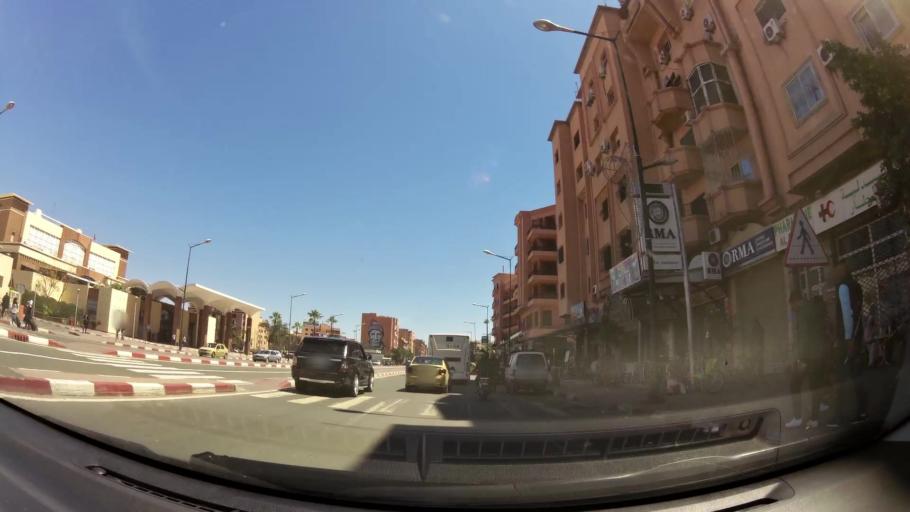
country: MA
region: Marrakech-Tensift-Al Haouz
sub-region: Marrakech
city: Marrakesh
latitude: 31.6296
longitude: -8.0176
